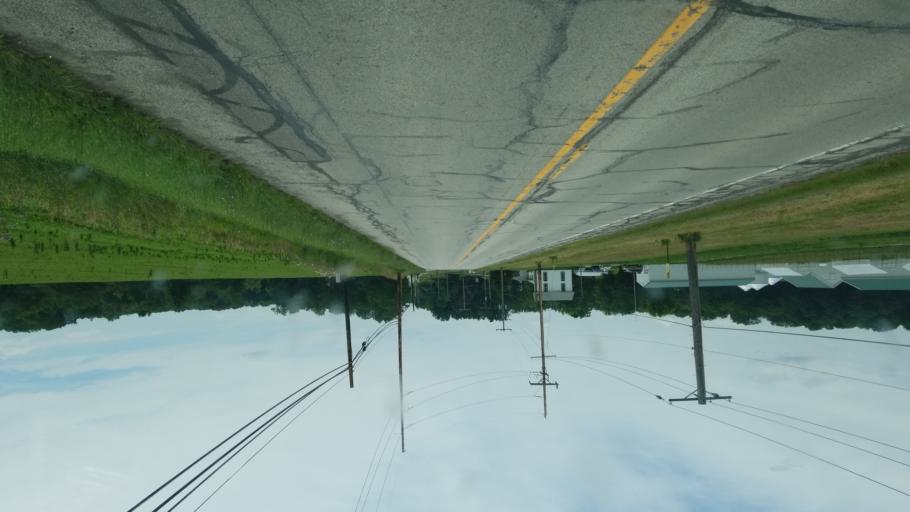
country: US
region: Ohio
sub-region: Geauga County
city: Bainbridge
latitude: 41.3882
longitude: -81.2724
